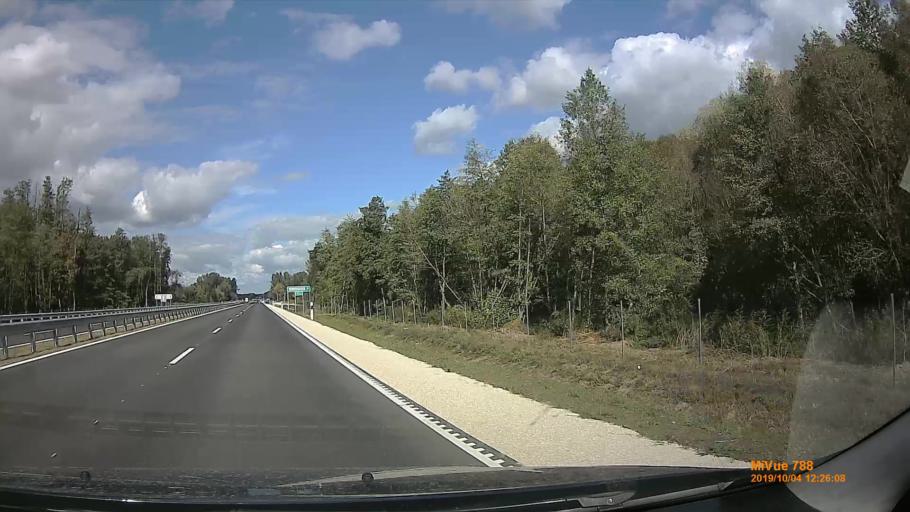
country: HU
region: Somogy
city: Karad
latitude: 46.6728
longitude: 17.7798
